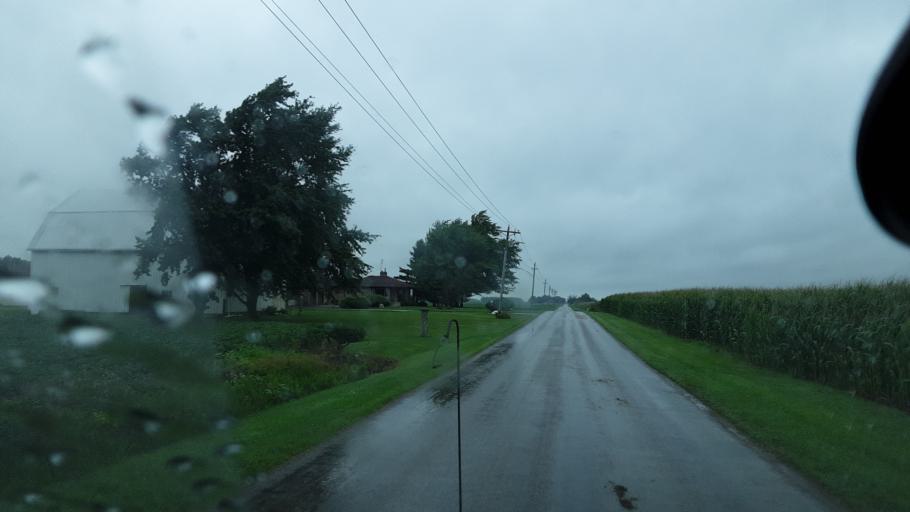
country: US
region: Indiana
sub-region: Adams County
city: Berne
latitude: 40.7278
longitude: -84.8539
